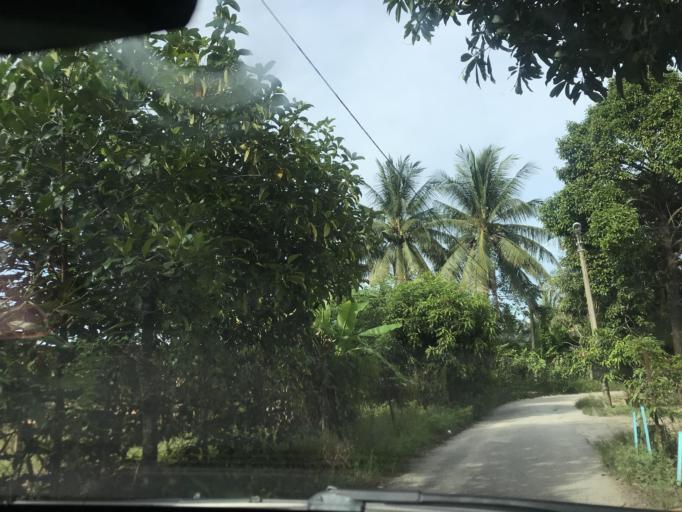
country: MY
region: Kelantan
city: Kota Bharu
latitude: 6.1326
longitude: 102.2162
